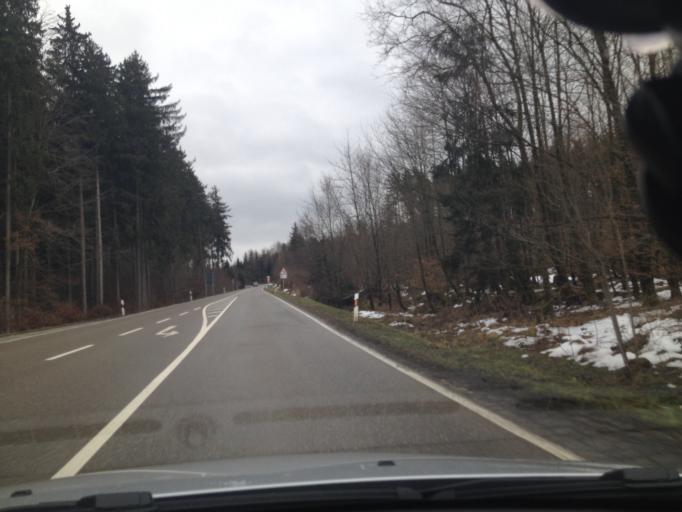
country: DE
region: Bavaria
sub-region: Swabia
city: Adelsried
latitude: 48.4091
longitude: 10.7334
